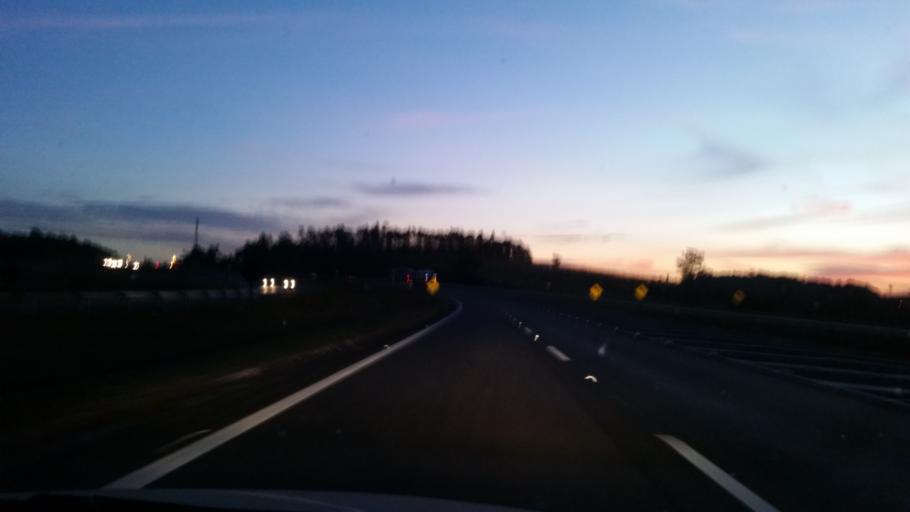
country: BR
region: Sao Paulo
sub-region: Santa Isabel
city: Santa Isabel
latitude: -23.3642
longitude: -46.1292
